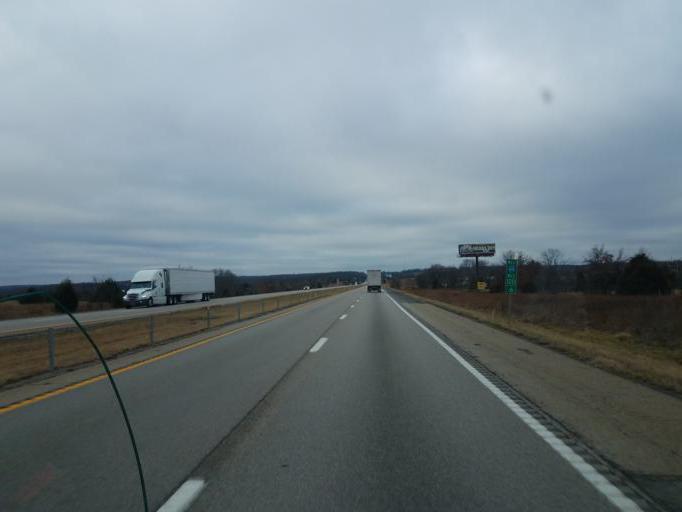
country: US
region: Missouri
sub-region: Laclede County
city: Lebanon
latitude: 37.5794
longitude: -92.7525
